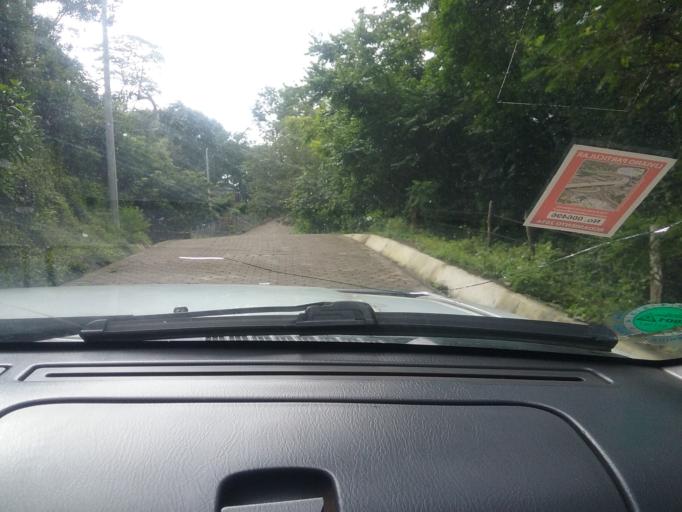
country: NI
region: Matagalpa
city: Matagalpa
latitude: 12.8724
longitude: -85.9448
